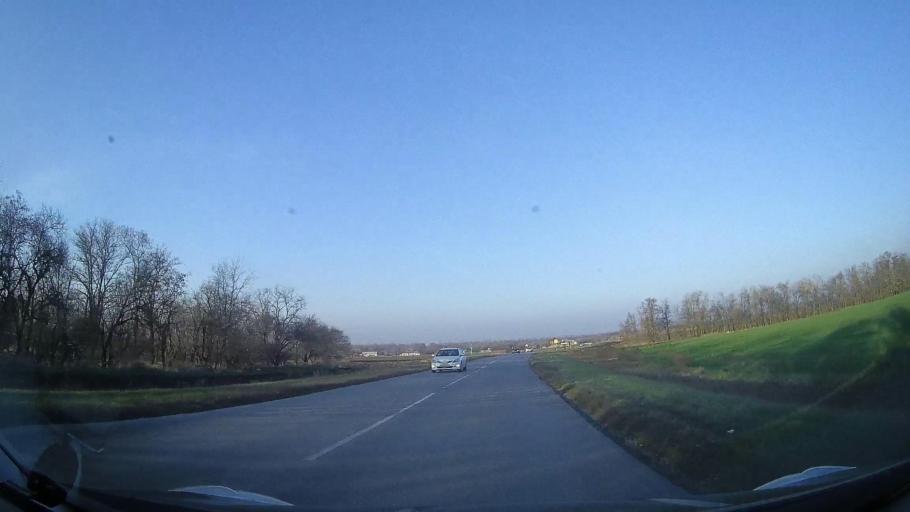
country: RU
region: Rostov
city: Kirovskaya
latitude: 47.0251
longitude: 39.9787
